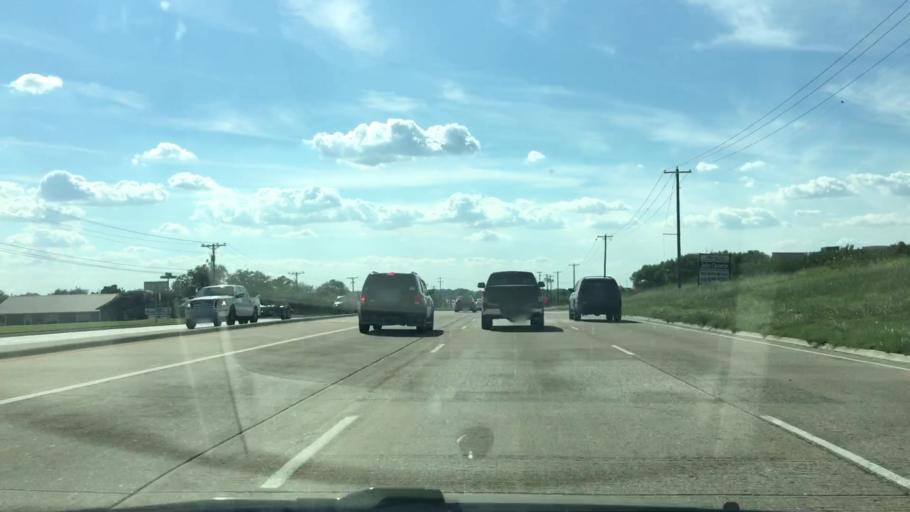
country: US
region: Texas
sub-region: Collin County
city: McKinney
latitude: 33.2181
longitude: -96.6747
